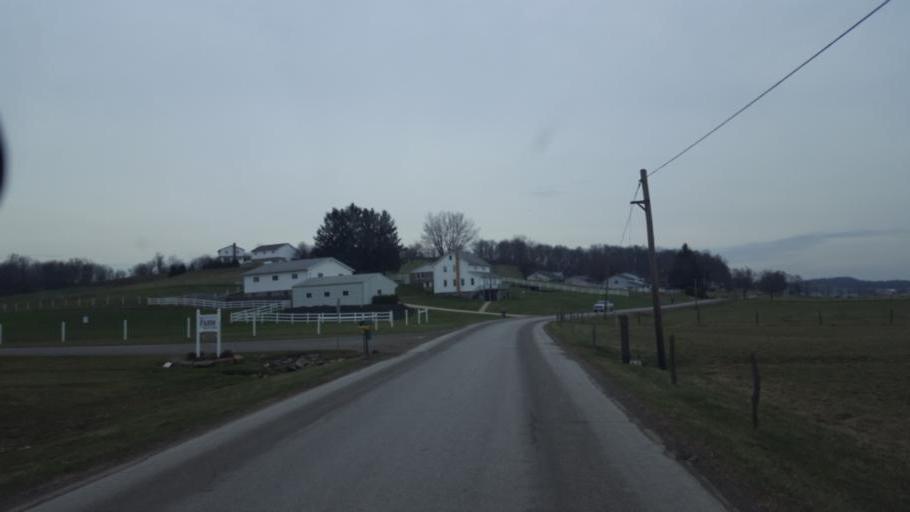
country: US
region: Ohio
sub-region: Tuscarawas County
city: Sugarcreek
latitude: 40.5205
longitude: -81.7353
